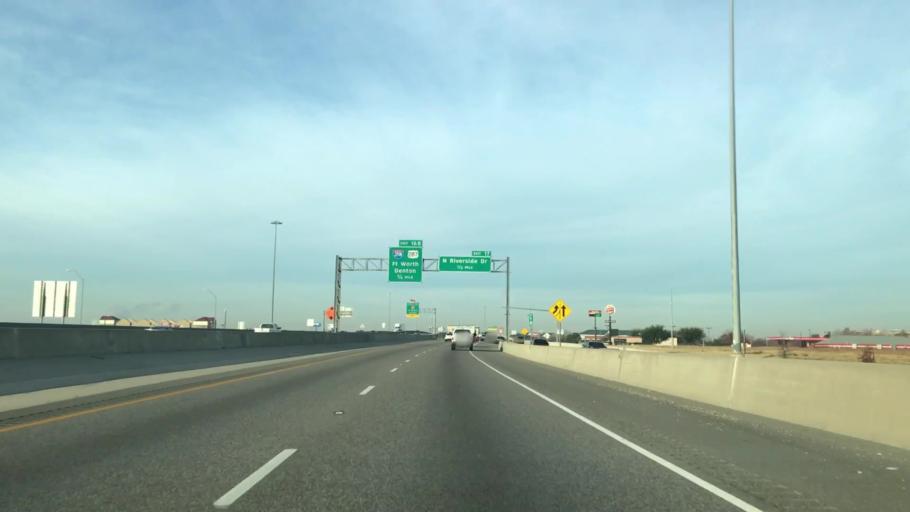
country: US
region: Texas
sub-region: Tarrant County
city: Watauga
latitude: 32.8398
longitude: -97.2861
